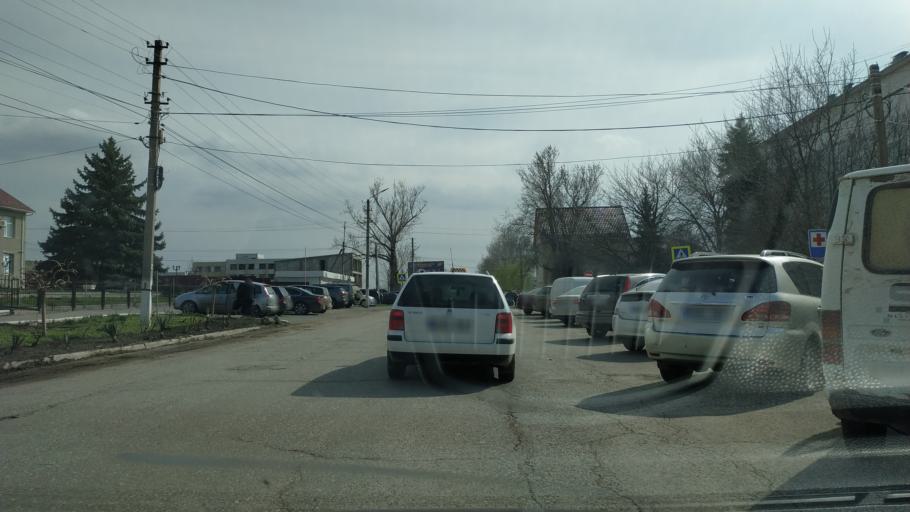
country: MD
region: Gagauzia
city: Vulcanesti
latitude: 45.6828
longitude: 28.4071
